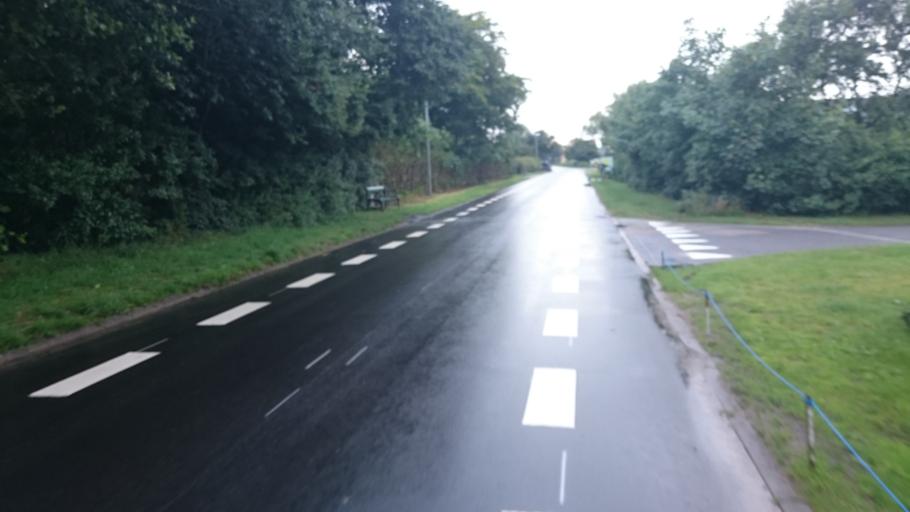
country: DK
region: South Denmark
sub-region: Fano Kommune
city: Nordby
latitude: 55.4396
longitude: 8.3937
